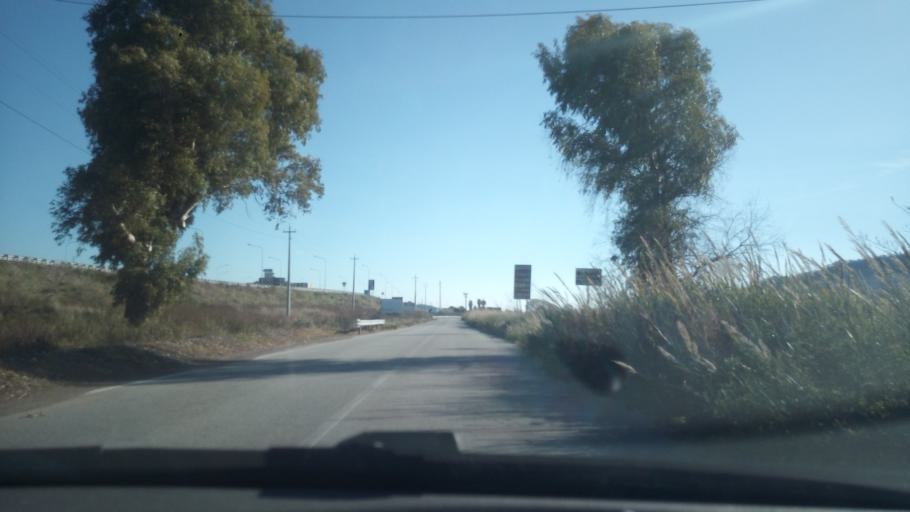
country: IT
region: Calabria
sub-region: Provincia di Catanzaro
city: Catanzaro
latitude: 38.8639
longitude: 16.5678
